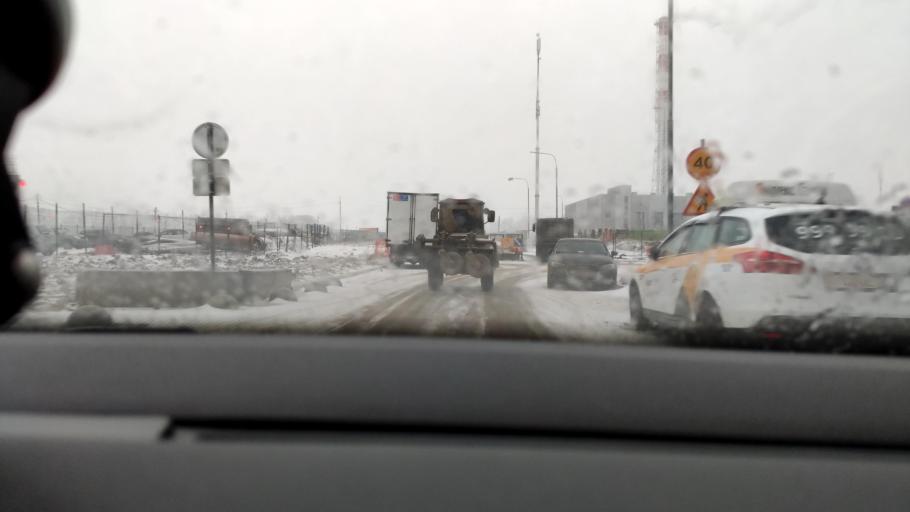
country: RU
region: Moskovskaya
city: Petrovskaya
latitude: 55.5575
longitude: 37.8082
